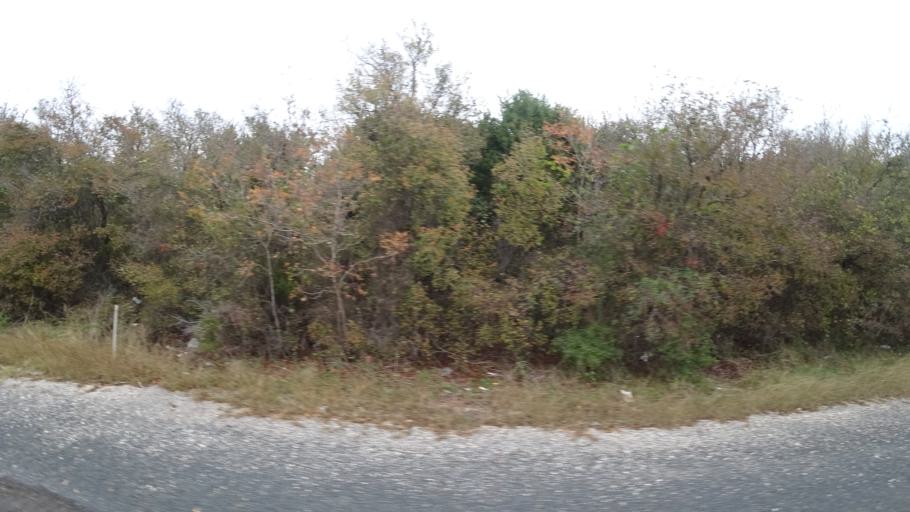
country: US
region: Texas
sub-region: Travis County
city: Pflugerville
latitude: 30.3996
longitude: -97.6005
